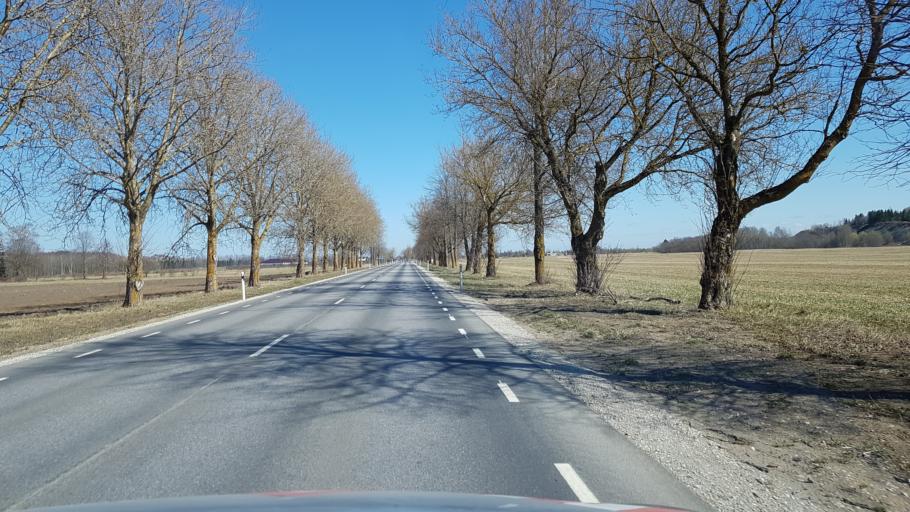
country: EE
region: Ida-Virumaa
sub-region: Johvi vald
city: Johvi
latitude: 59.3450
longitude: 27.3641
